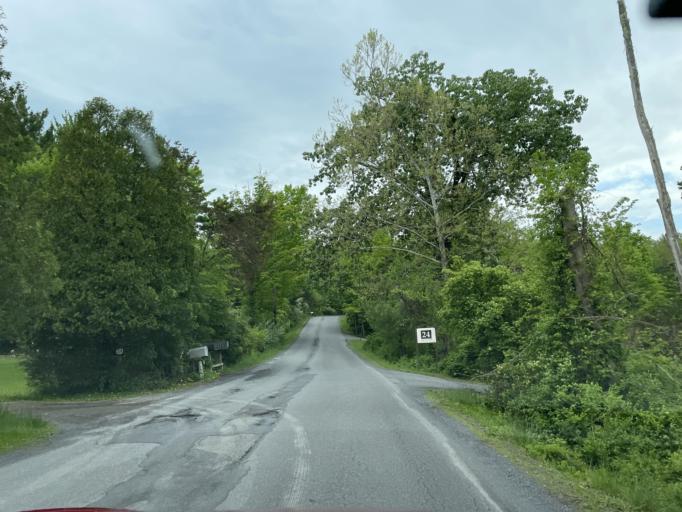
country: US
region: New York
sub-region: Ulster County
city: Woodstock
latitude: 42.0328
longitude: -74.1276
